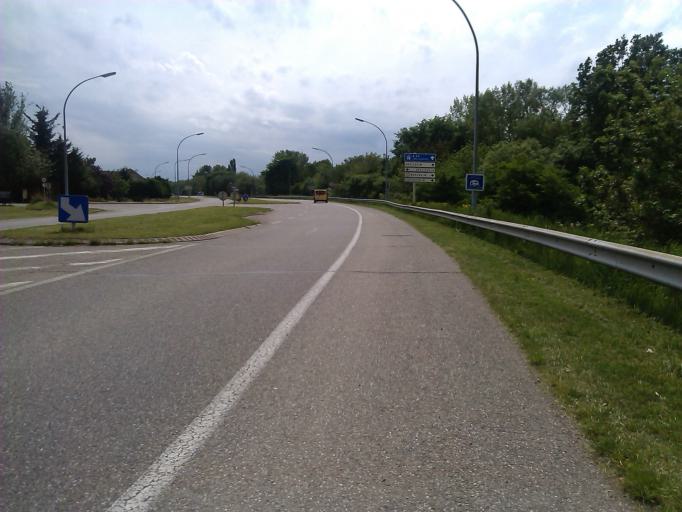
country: FR
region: Alsace
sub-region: Departement du Haut-Rhin
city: Reguisheim
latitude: 47.8995
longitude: 7.3539
